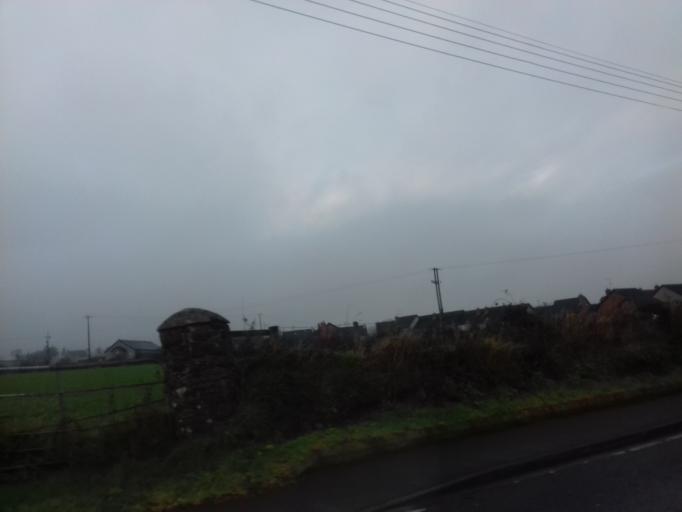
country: GB
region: Northern Ireland
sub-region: Strabane District
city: Sion Mills
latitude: 54.7803
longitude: -7.4693
